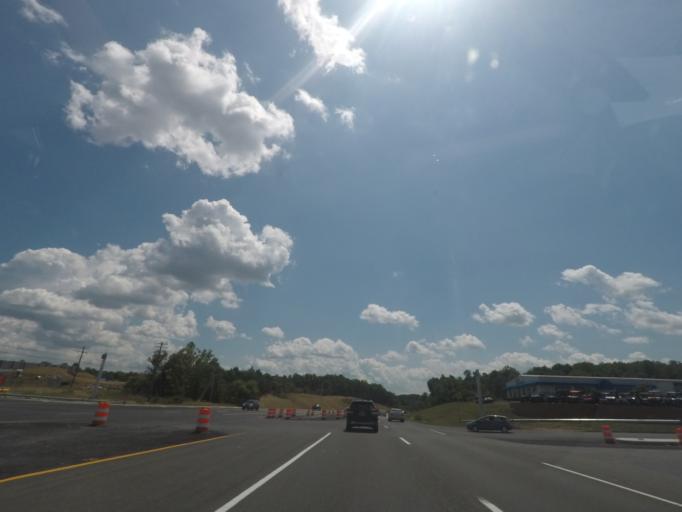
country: US
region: Virginia
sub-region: City of Winchester
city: Winchester
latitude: 39.1408
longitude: -78.1246
